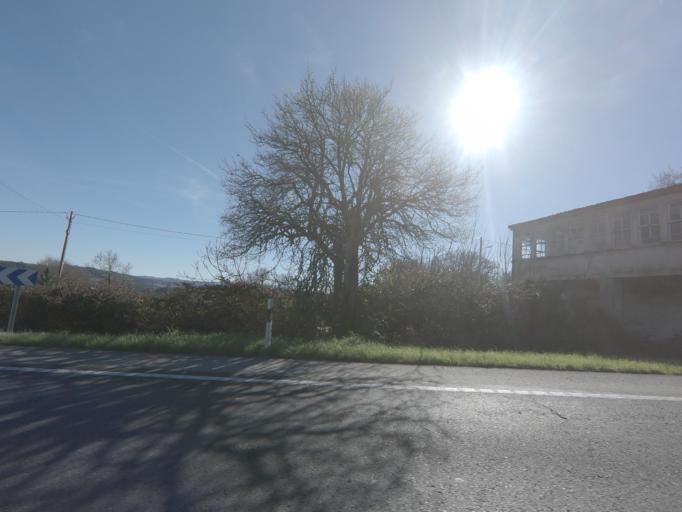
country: ES
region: Galicia
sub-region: Provincia de Pontevedra
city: Silleda
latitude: 42.6860
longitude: -8.2170
